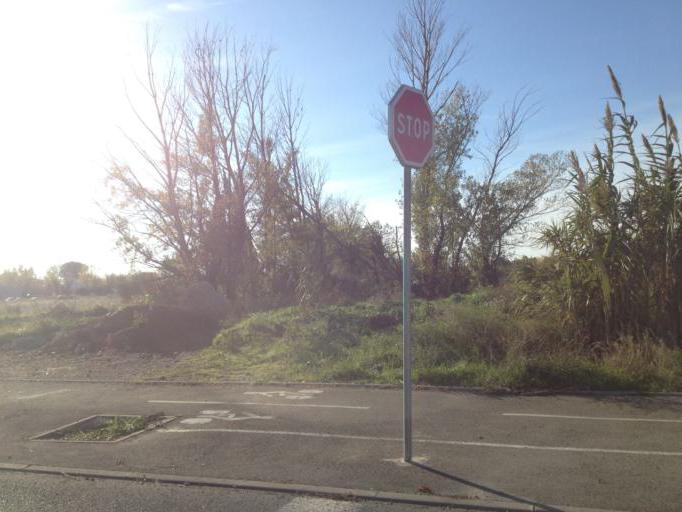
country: FR
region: Provence-Alpes-Cote d'Azur
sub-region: Departement des Bouches-du-Rhone
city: Istres
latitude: 43.5058
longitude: 4.9677
